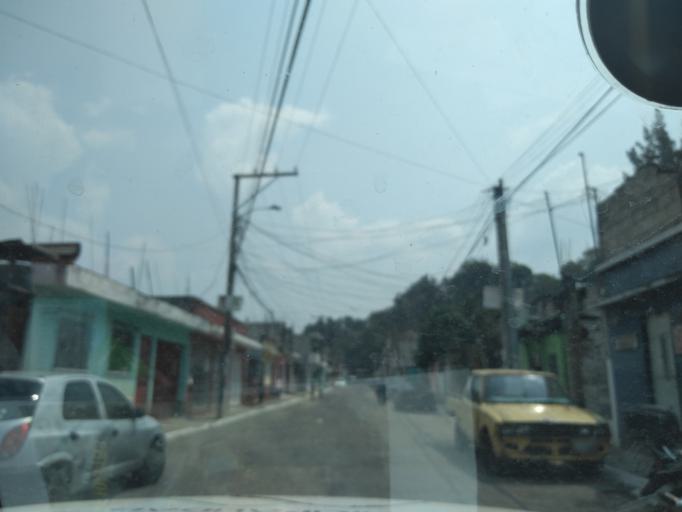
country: GT
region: Guatemala
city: Petapa
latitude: 14.5186
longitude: -90.5412
